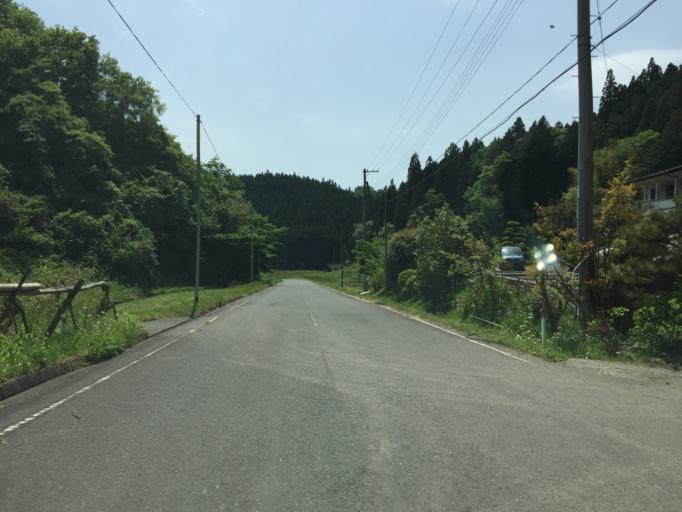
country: JP
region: Fukushima
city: Ishikawa
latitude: 37.1683
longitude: 140.5012
